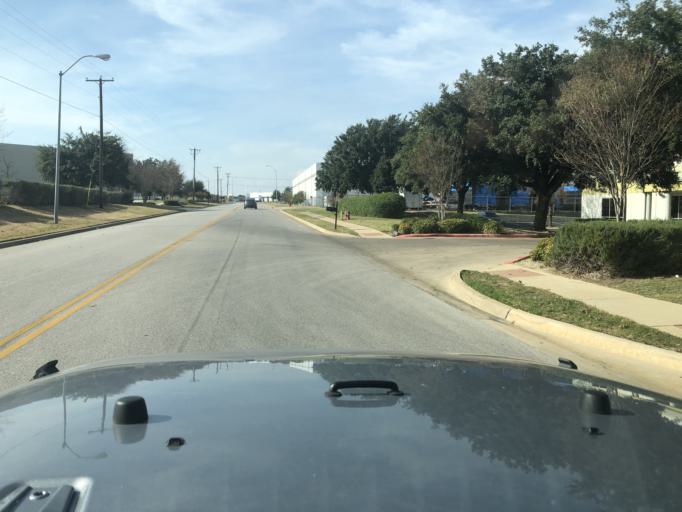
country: US
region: Texas
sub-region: Williamson County
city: Round Rock
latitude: 30.5370
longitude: -97.6853
